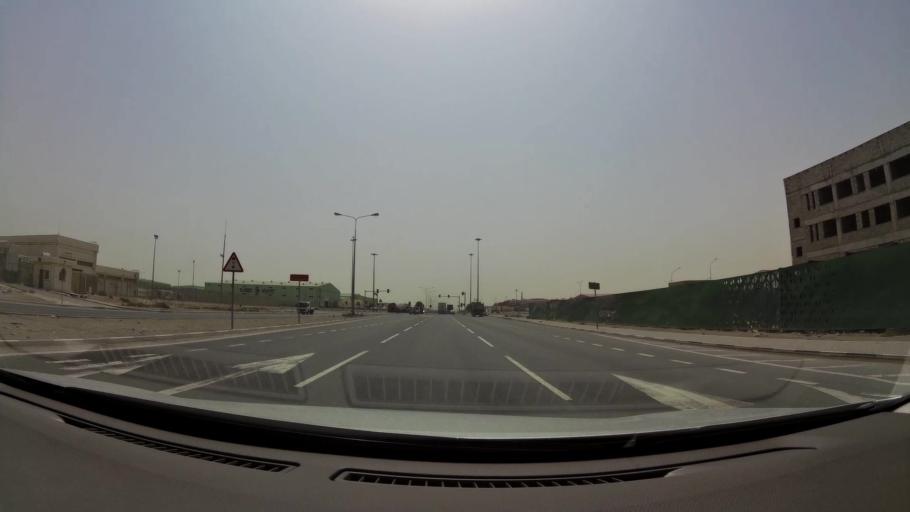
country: QA
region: Al Wakrah
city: Al Wukayr
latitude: 25.1605
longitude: 51.4078
